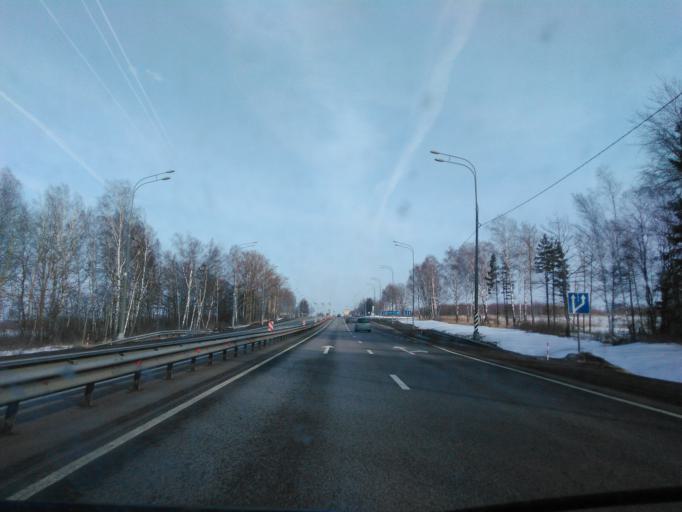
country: RU
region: Smolensk
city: Safonovo
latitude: 55.1268
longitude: 33.1383
